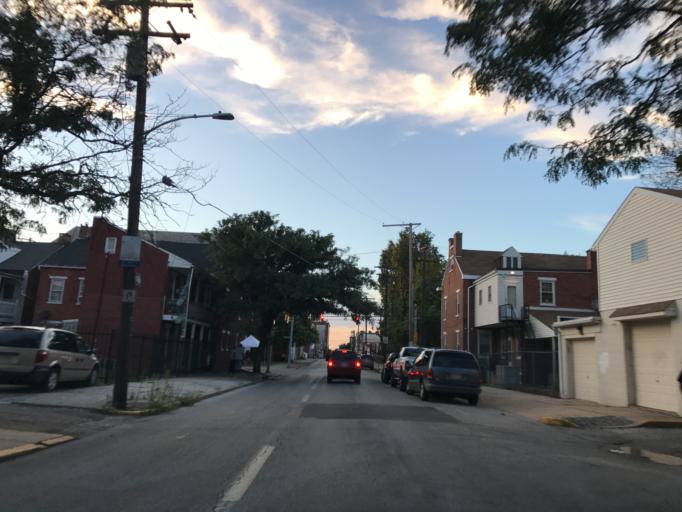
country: US
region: Pennsylvania
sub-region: York County
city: York
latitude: 39.9583
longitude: -76.7234
